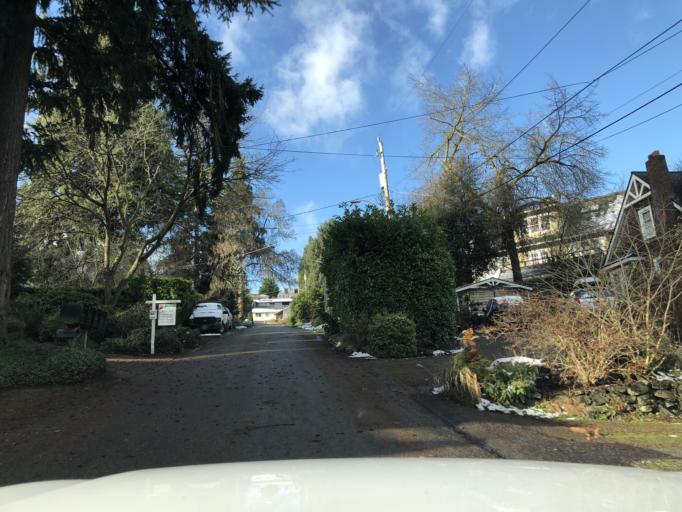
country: US
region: Washington
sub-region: King County
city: Lake Forest Park
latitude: 47.7182
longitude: -122.2812
